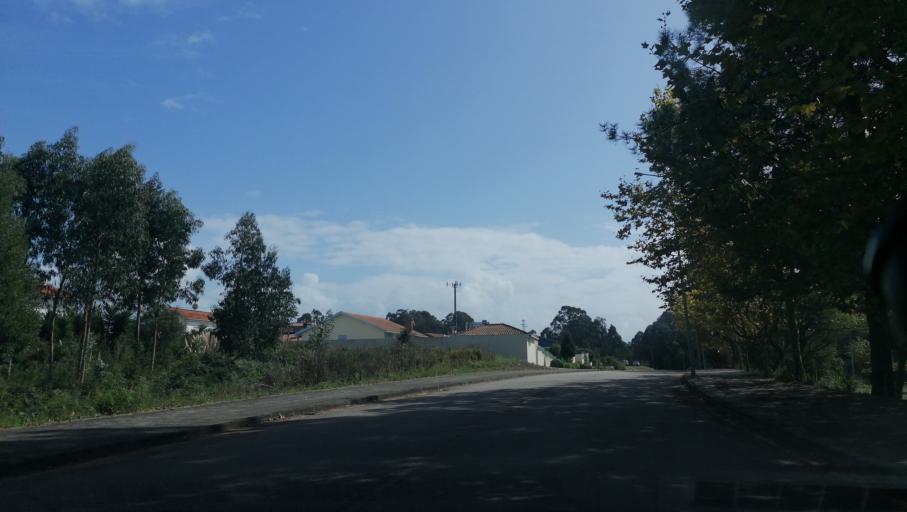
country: PT
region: Aveiro
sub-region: Espinho
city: Silvalde
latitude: 40.9999
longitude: -8.6209
